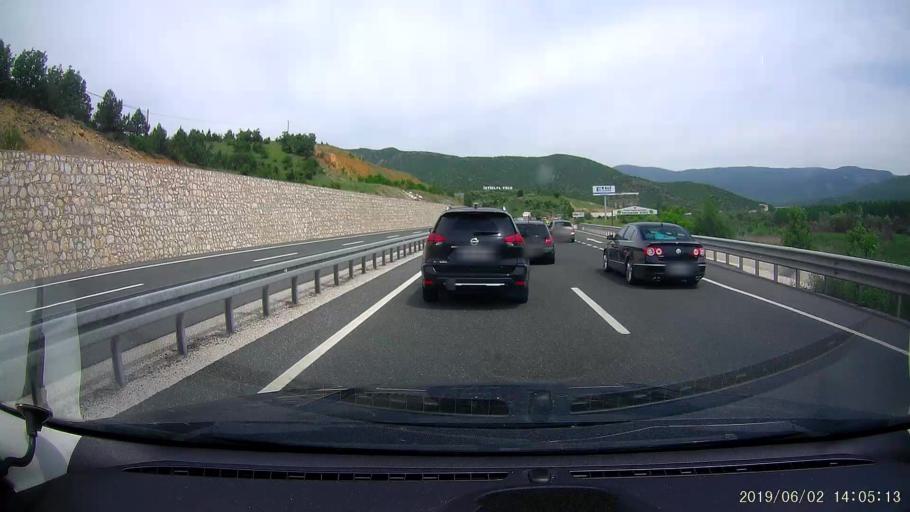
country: TR
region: Cankiri
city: Ilgaz
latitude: 40.9022
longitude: 33.6656
